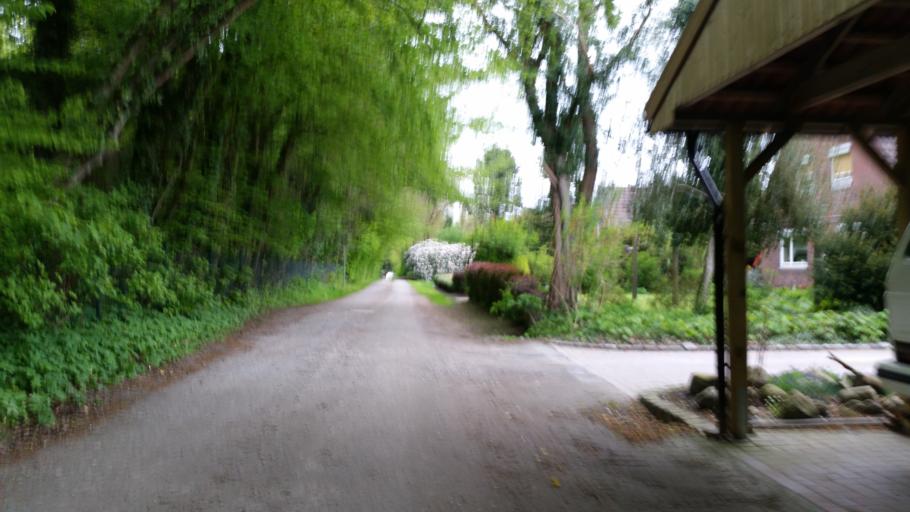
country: DE
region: Lower Saxony
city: Aurich
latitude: 53.4740
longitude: 7.4632
